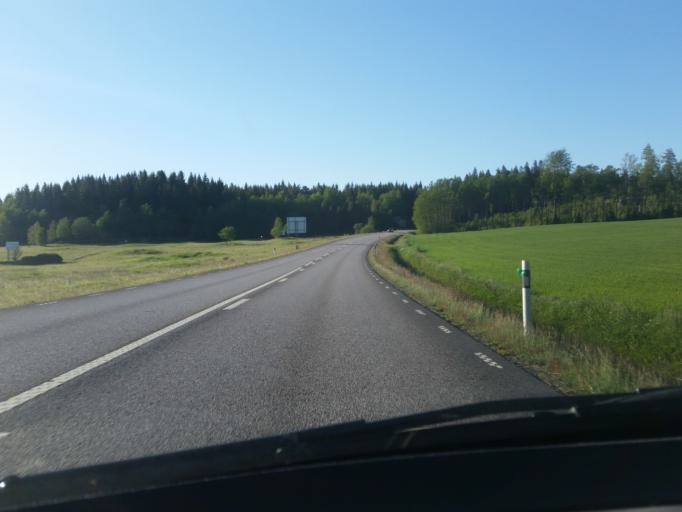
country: SE
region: Vaestra Goetaland
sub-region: Fargelanda Kommun
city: Faergelanda
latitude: 58.5224
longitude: 11.9787
